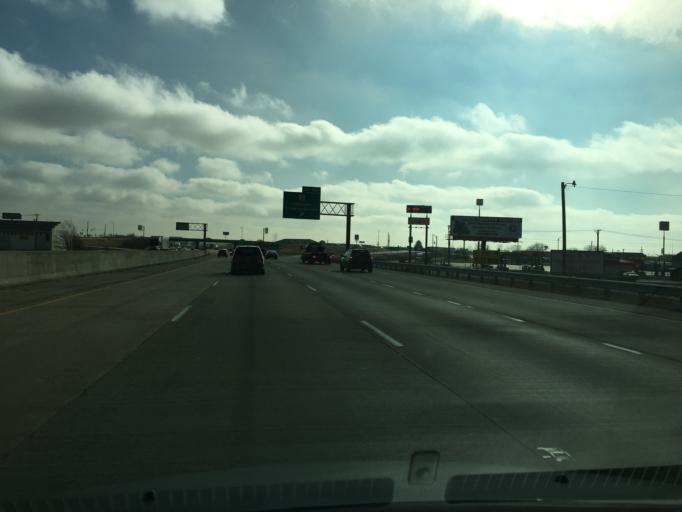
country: US
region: Indiana
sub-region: Boone County
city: Lebanon
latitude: 40.0502
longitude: -86.4917
